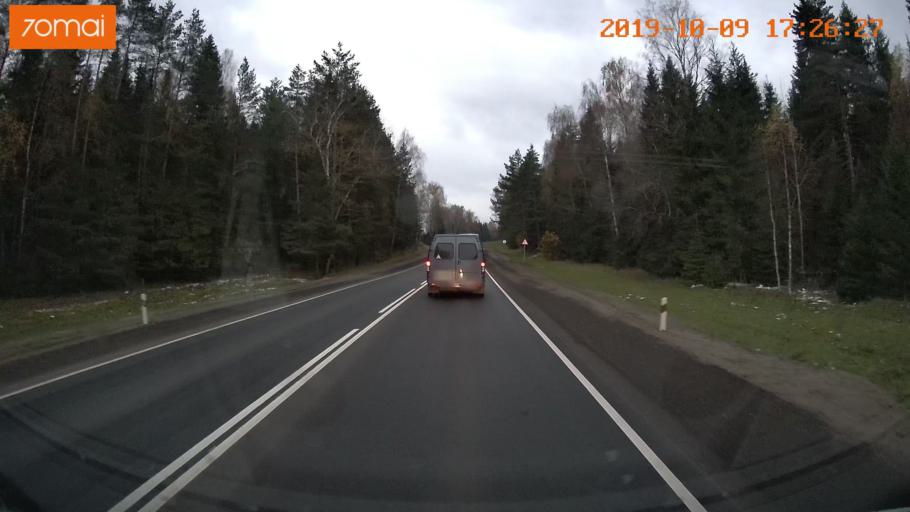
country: RU
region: Ivanovo
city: Furmanov
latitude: 57.1734
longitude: 41.0802
